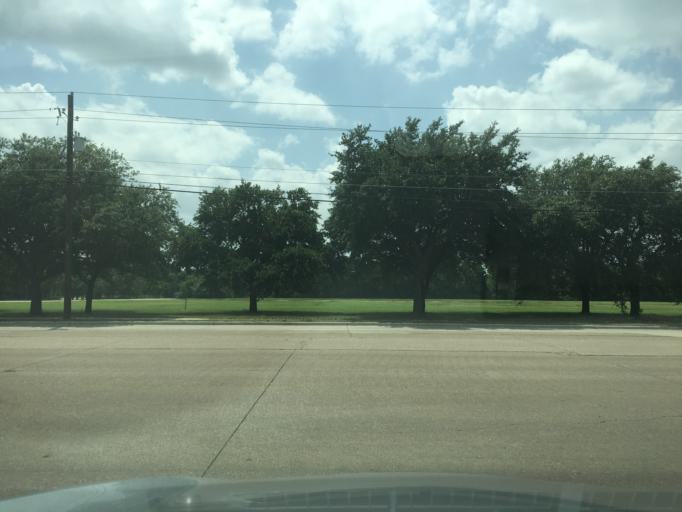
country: US
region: Texas
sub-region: Dallas County
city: Addison
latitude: 32.9079
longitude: -96.8176
